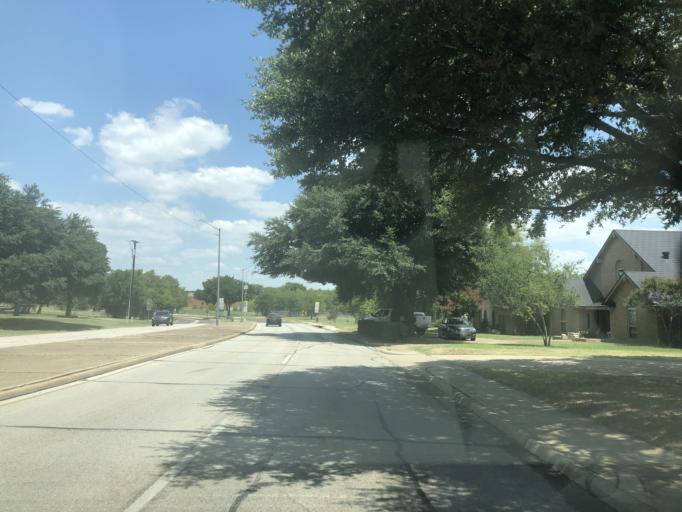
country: US
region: Texas
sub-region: Dallas County
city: Grand Prairie
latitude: 32.7666
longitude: -97.0200
